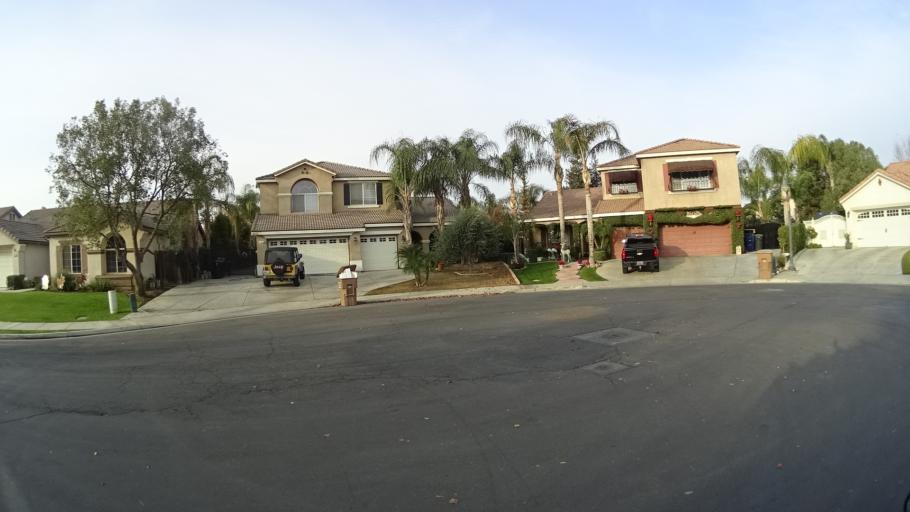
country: US
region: California
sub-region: Kern County
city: Greenacres
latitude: 35.4220
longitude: -119.1218
